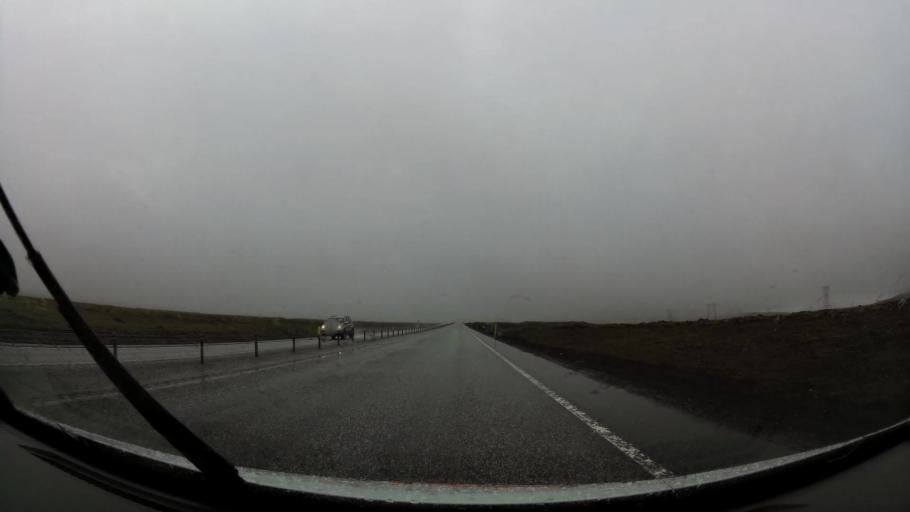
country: IS
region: South
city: Hveragerdi
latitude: 64.0179
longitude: -21.2808
